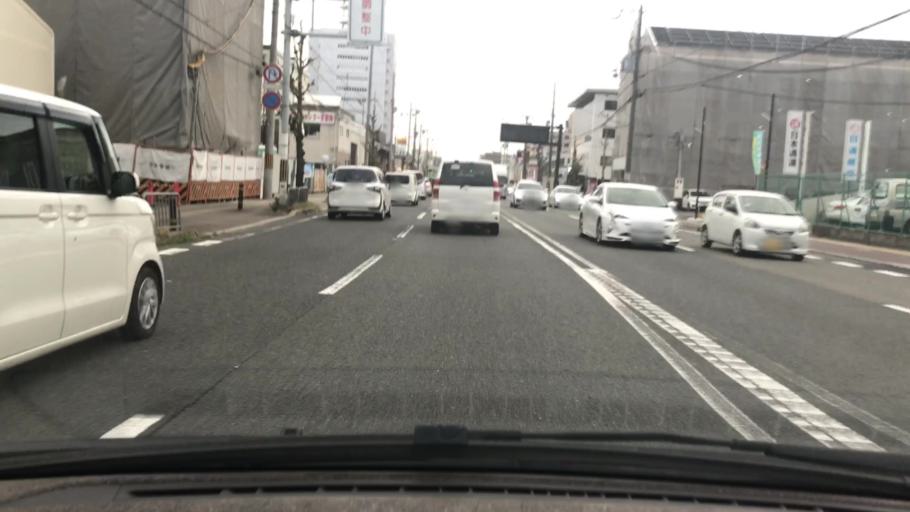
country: JP
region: Kyoto
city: Muko
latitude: 34.9641
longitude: 135.7458
